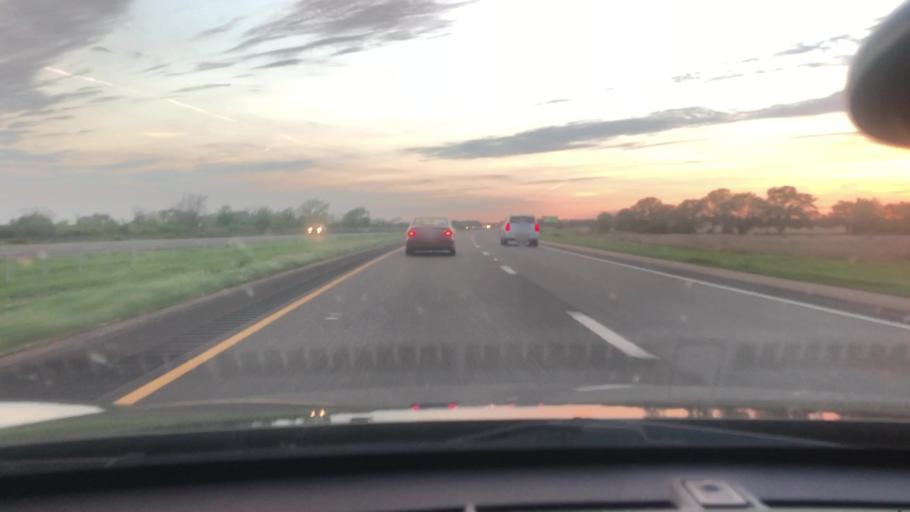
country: US
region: Texas
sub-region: Victoria County
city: Inez
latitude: 28.9246
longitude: -96.7526
